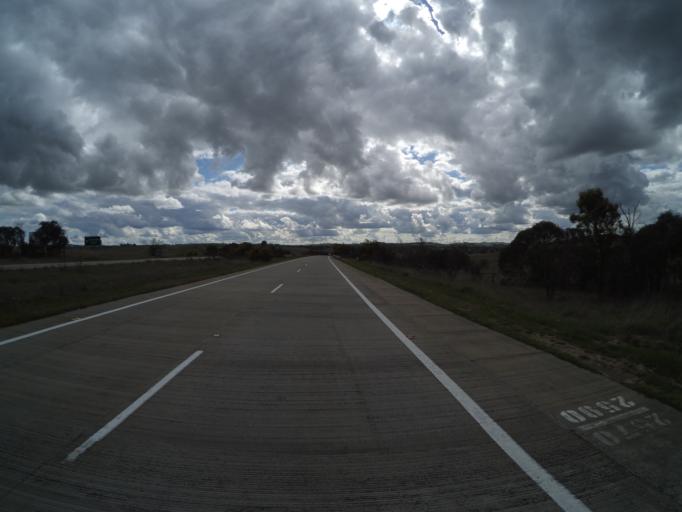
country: AU
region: New South Wales
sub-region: Yass Valley
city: Gundaroo
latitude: -34.7977
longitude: 149.2804
